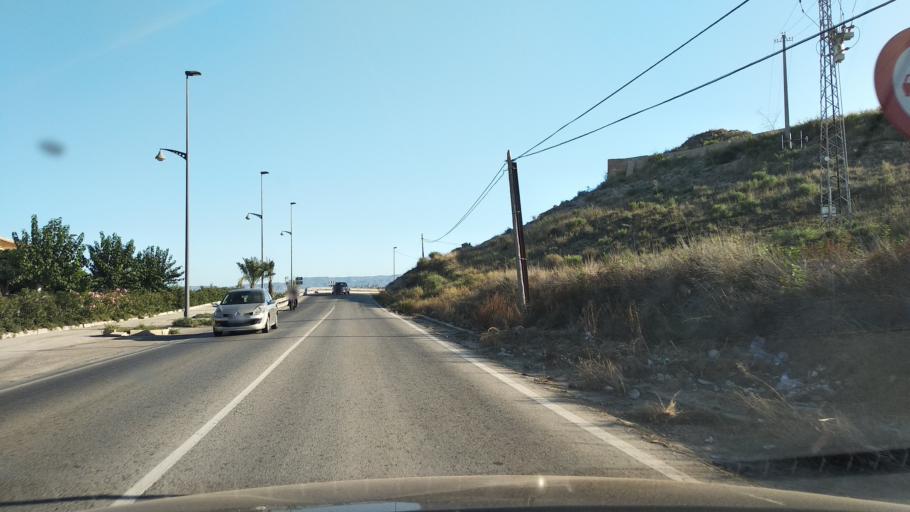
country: ES
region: Murcia
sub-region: Murcia
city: Santomera
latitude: 38.0572
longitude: -1.0529
